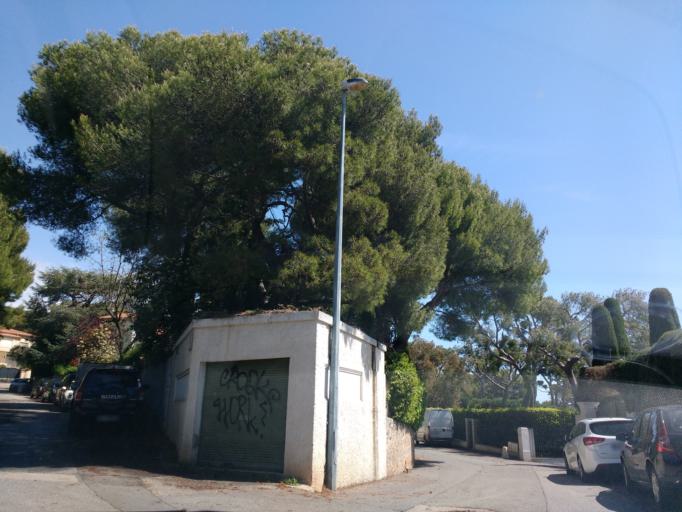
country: FR
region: Provence-Alpes-Cote d'Azur
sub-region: Departement des Alpes-Maritimes
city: Saint-Jean-Cap-Ferrat
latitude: 43.6760
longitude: 7.3276
